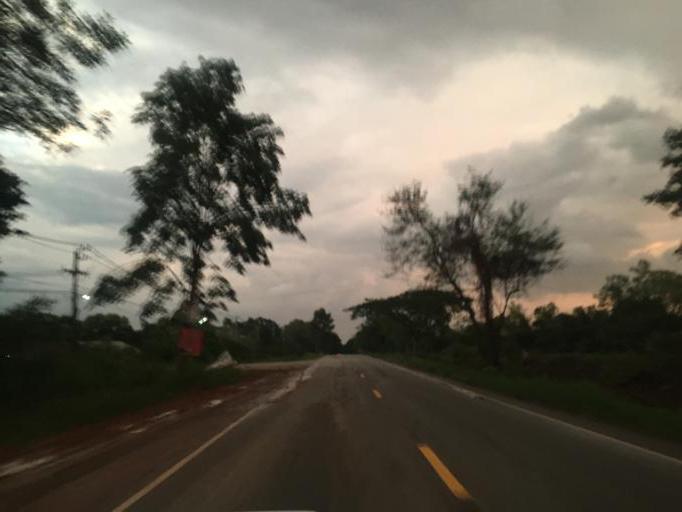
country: TH
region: Changwat Udon Thani
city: Udon Thani
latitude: 17.3428
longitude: 102.7174
